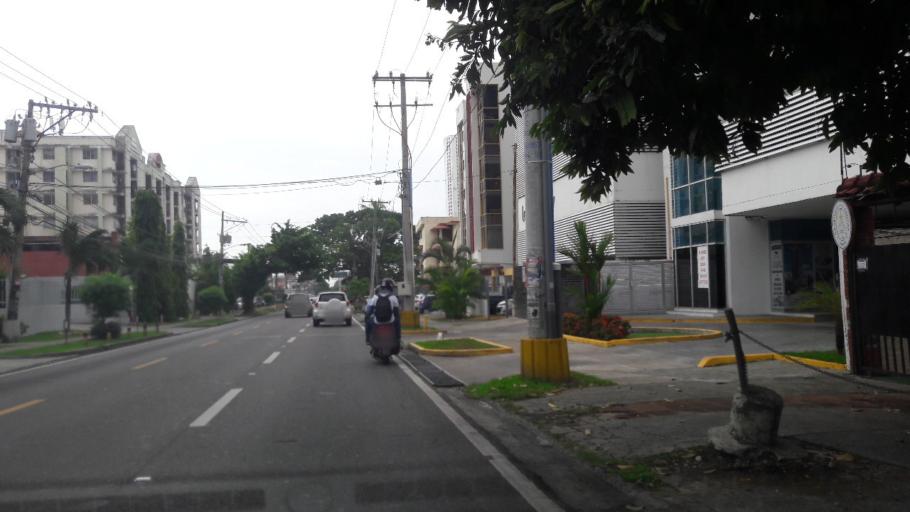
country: PA
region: Panama
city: Panama
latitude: 9.0063
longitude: -79.5002
